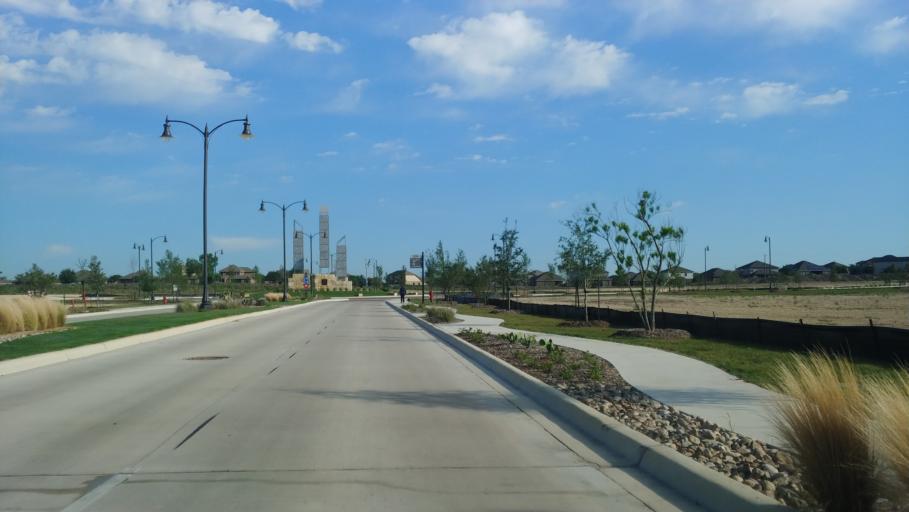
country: US
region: Texas
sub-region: Bexar County
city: Live Oak
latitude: 29.5645
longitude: -98.3425
